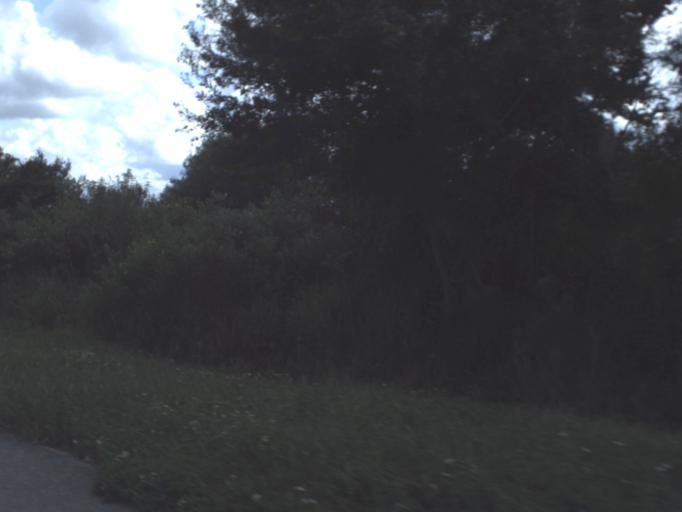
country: US
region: Florida
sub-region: Hardee County
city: Bowling Green
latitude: 27.5949
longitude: -81.9946
